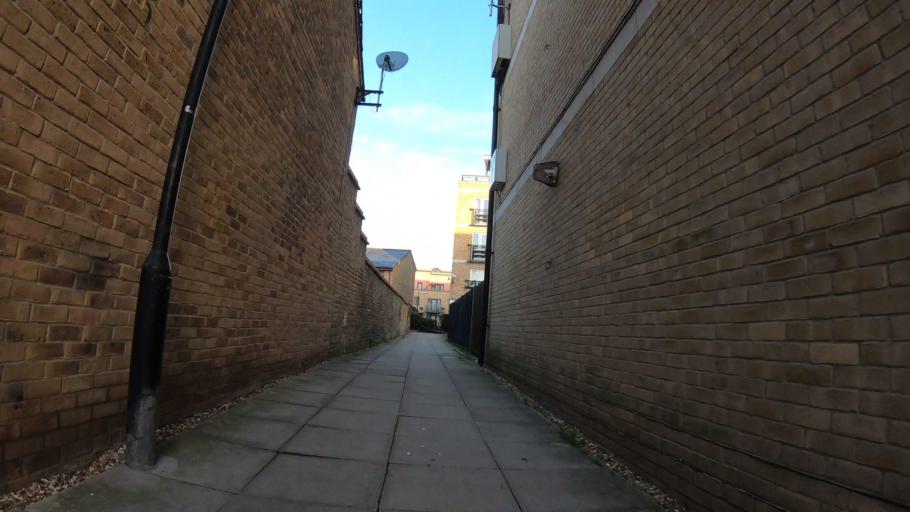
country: GB
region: England
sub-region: Greater London
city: Poplar
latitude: 51.5150
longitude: -0.0241
